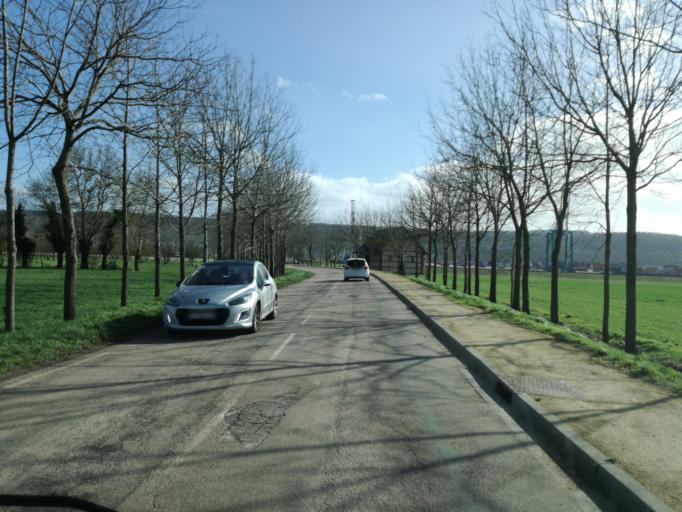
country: FR
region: Haute-Normandie
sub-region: Departement de la Seine-Maritime
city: Grand-Couronne
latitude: 49.3590
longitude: 0.9801
